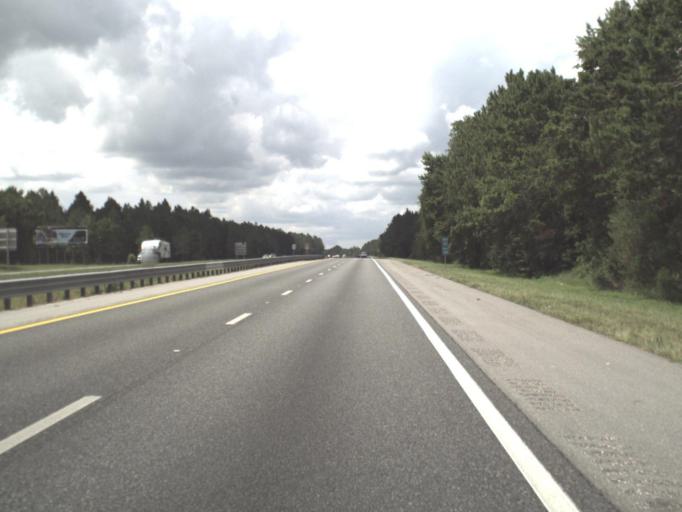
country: US
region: Florida
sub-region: Hernando County
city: Hill 'n Dale
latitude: 28.5101
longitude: -82.2422
